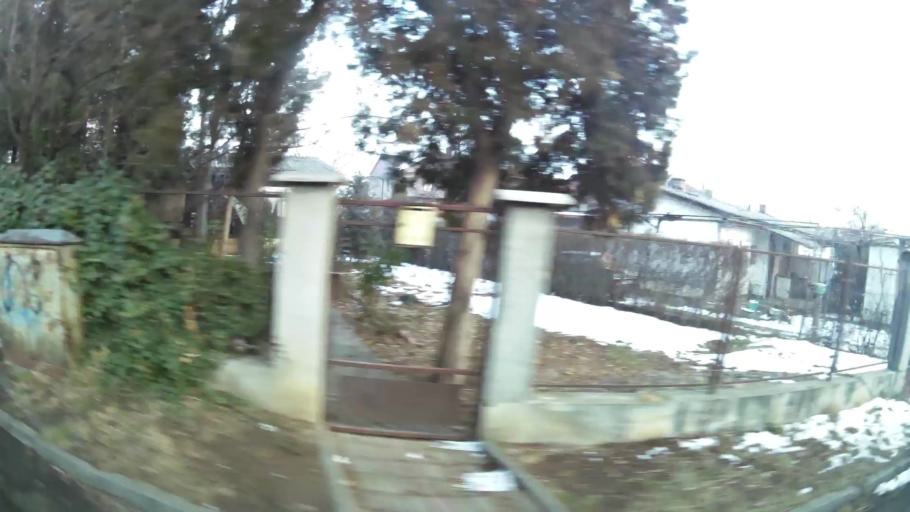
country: MK
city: Creshevo
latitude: 42.0085
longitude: 21.5090
